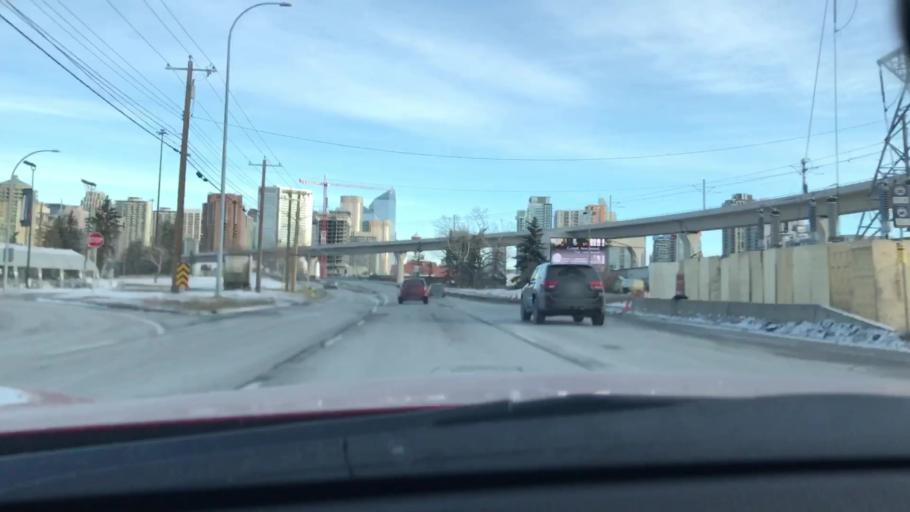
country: CA
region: Alberta
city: Calgary
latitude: 51.0453
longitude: -114.0976
